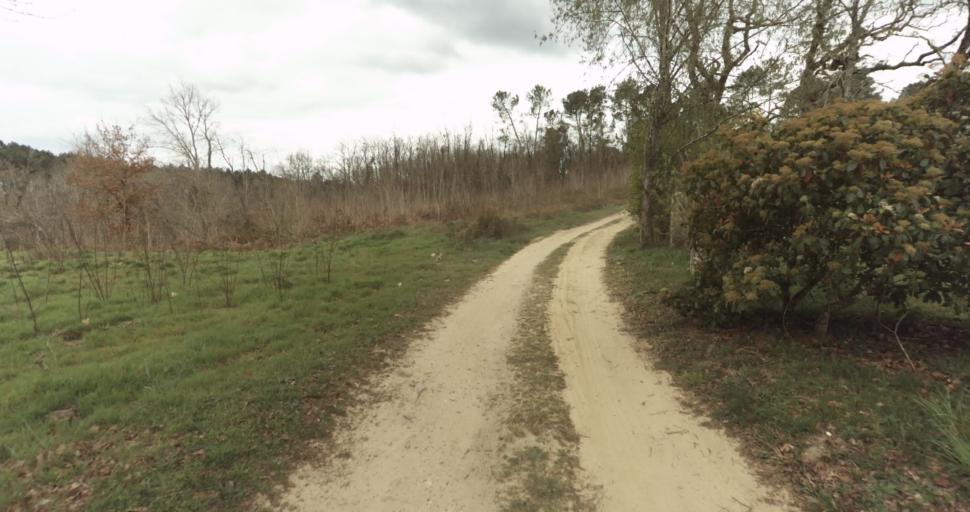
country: FR
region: Aquitaine
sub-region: Departement des Landes
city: Sarbazan
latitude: 44.0241
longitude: -0.3084
